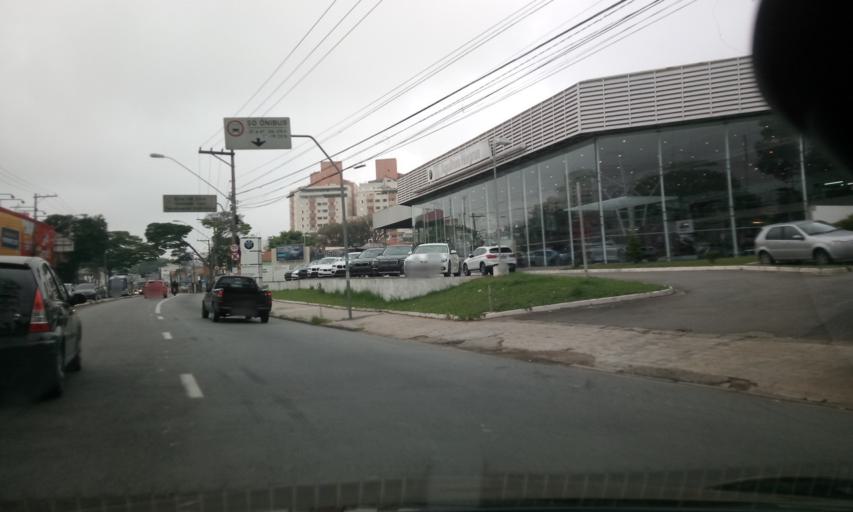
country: BR
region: Sao Paulo
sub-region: Sao Caetano Do Sul
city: Sao Caetano do Sul
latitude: -23.6494
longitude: -46.5781
